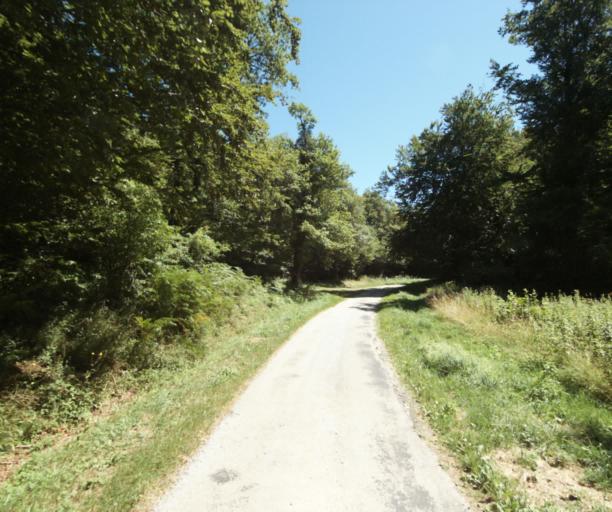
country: FR
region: Midi-Pyrenees
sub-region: Departement du Tarn
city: Dourgne
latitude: 43.4307
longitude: 2.1538
